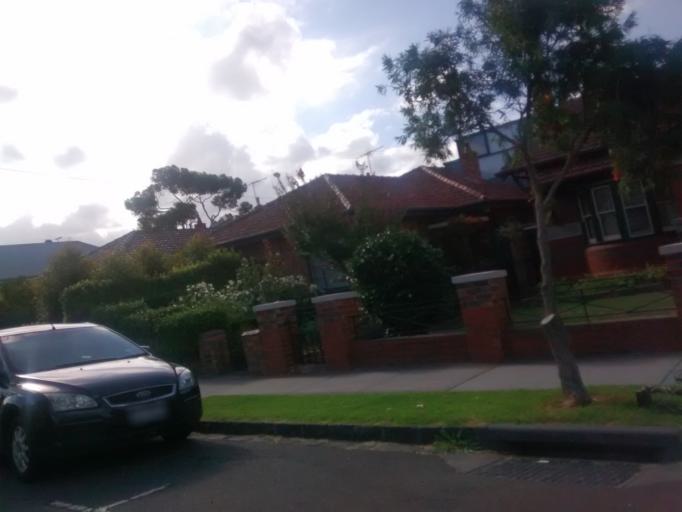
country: AU
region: Victoria
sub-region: Yarra
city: North Fitzroy
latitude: -37.7769
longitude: 144.9850
